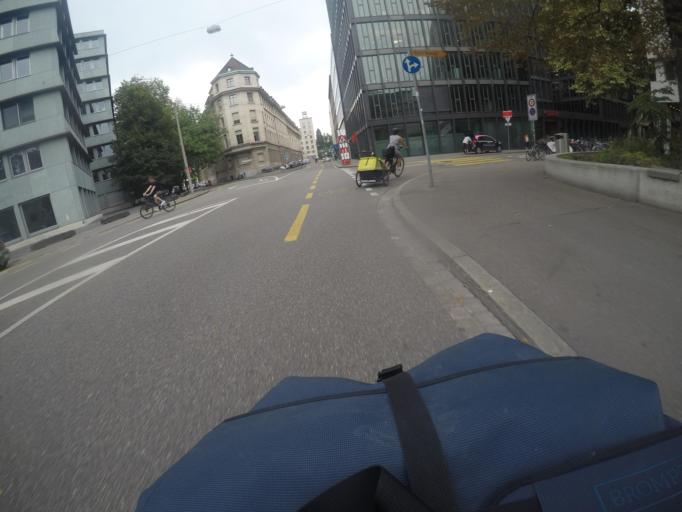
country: CH
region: Basel-City
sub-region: Basel-Stadt
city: Basel
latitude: 47.5532
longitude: 7.5949
